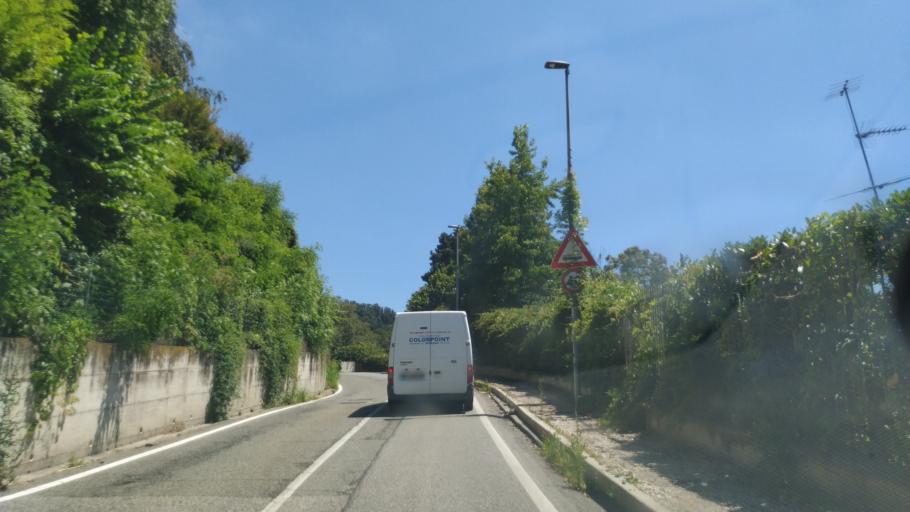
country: IT
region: Piedmont
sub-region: Provincia di Torino
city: San Mauro Torinese
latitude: 45.0834
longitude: 7.7407
